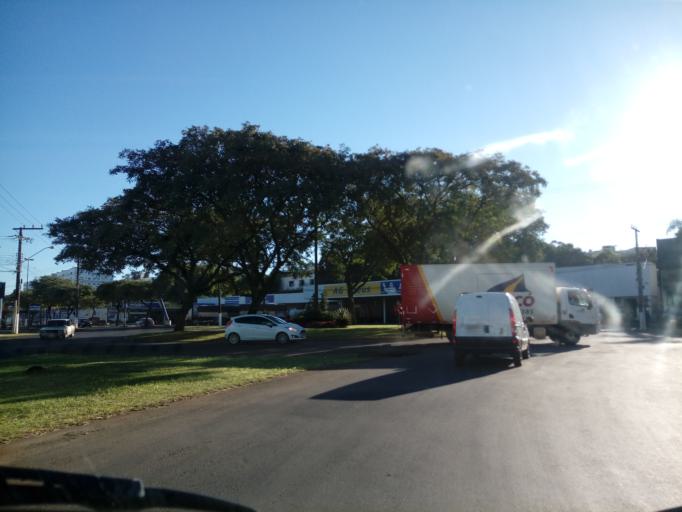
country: BR
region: Santa Catarina
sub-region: Chapeco
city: Chapeco
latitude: -27.0878
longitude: -52.6217
